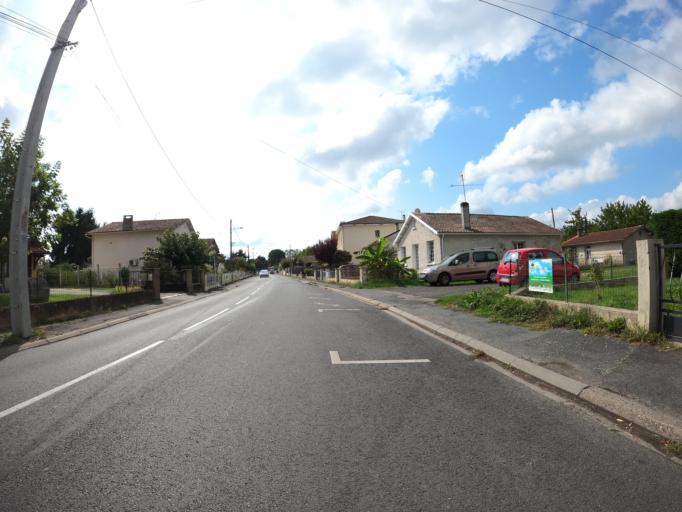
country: FR
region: Aquitaine
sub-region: Departement de la Dordogne
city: Bergerac
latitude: 44.8416
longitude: 0.4831
